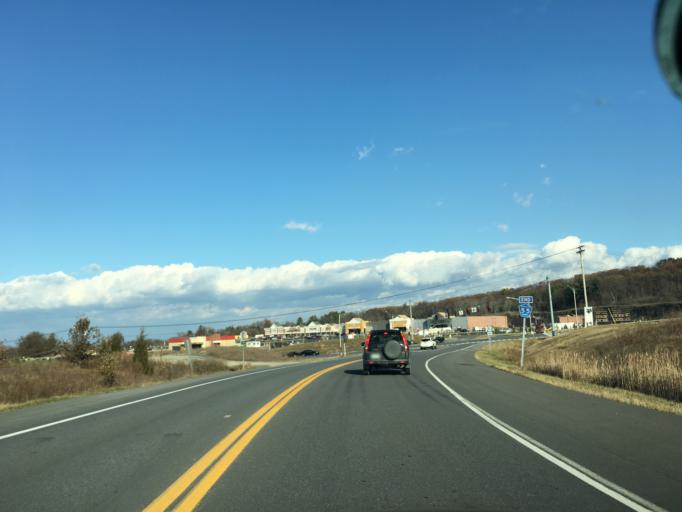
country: US
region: New York
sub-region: Rensselaer County
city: Hampton Manor
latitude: 42.6522
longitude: -73.6917
